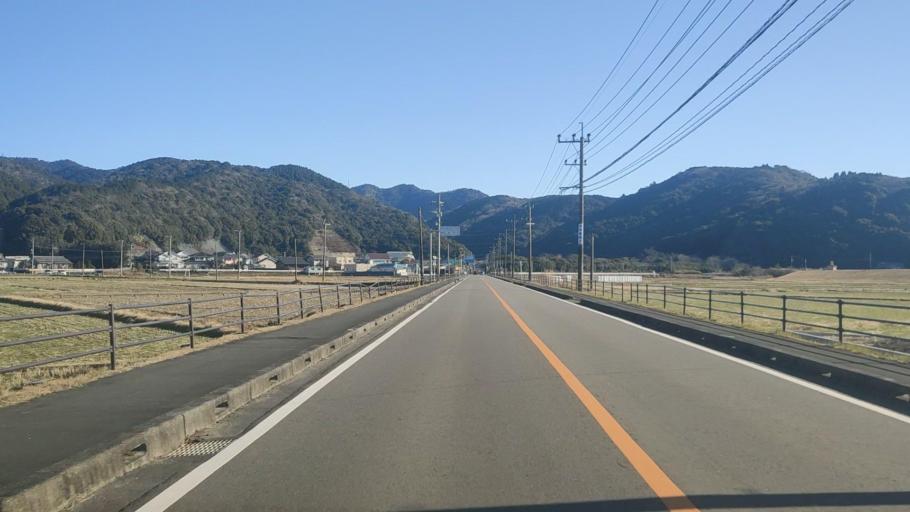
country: JP
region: Miyazaki
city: Nobeoka
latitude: 32.6162
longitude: 131.6957
